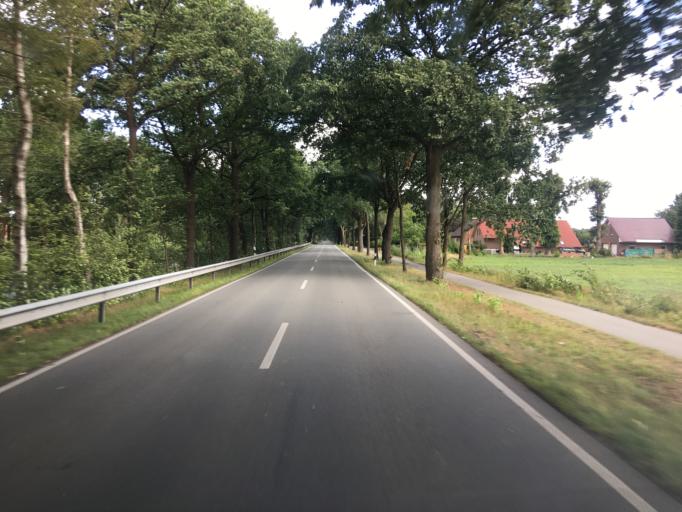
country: DE
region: Lower Saxony
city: Friesoythe
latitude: 53.0858
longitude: 7.8054
